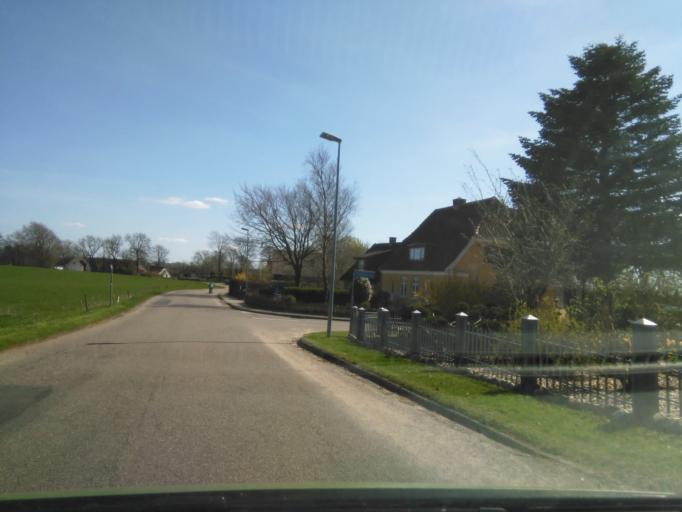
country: DK
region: Central Jutland
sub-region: Silkeborg Kommune
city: Kjellerup
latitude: 56.3525
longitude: 9.3387
